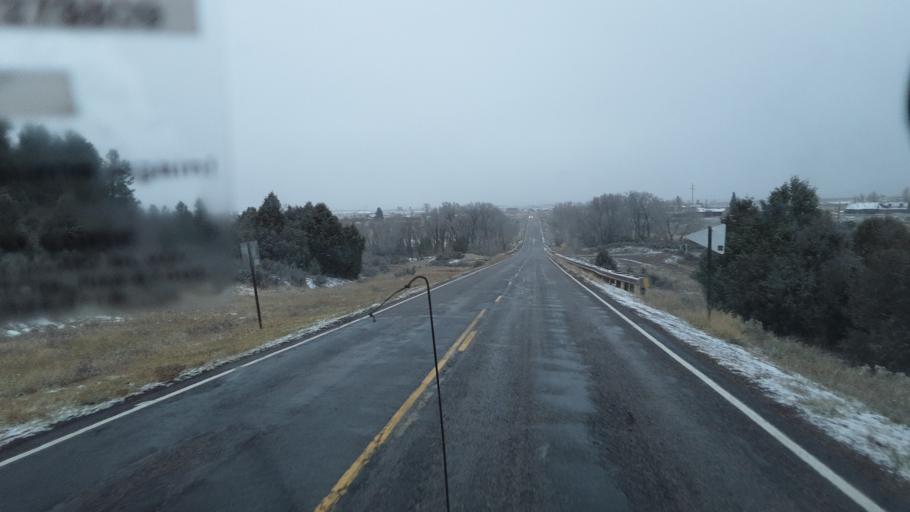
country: US
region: New Mexico
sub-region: Rio Arriba County
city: Tierra Amarilla
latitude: 36.6965
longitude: -106.5582
